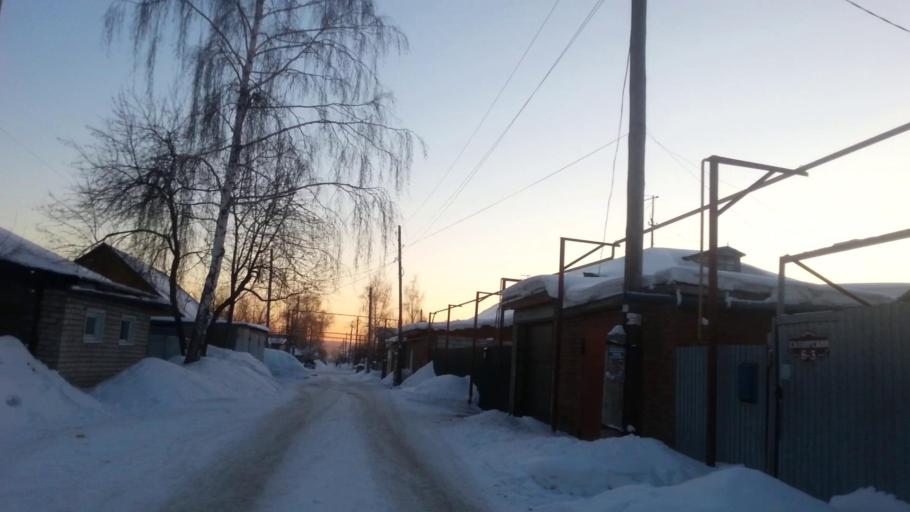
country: RU
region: Altai Krai
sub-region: Gorod Barnaulskiy
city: Barnaul
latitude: 53.3534
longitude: 83.7044
